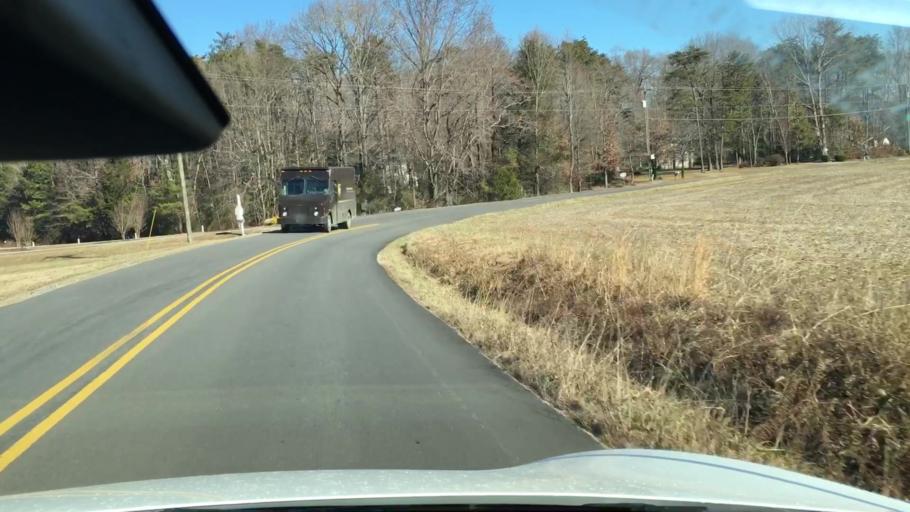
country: US
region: Virginia
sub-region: Powhatan County
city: Powhatan
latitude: 37.5693
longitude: -77.7836
